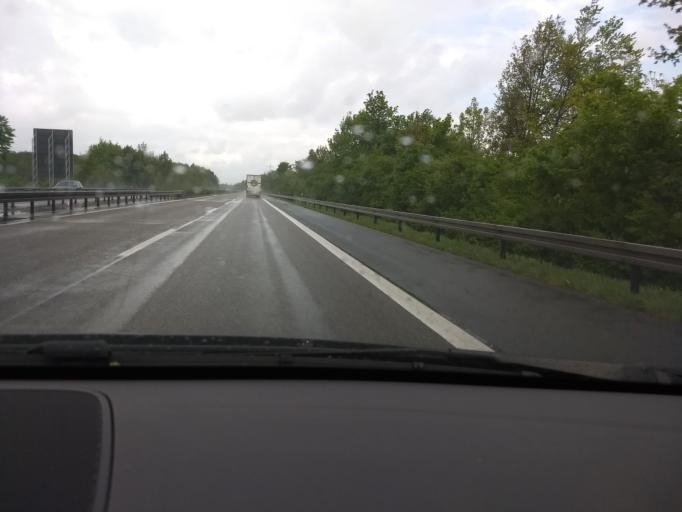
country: DE
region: North Rhine-Westphalia
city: Dorsten
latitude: 51.6372
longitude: 6.9332
